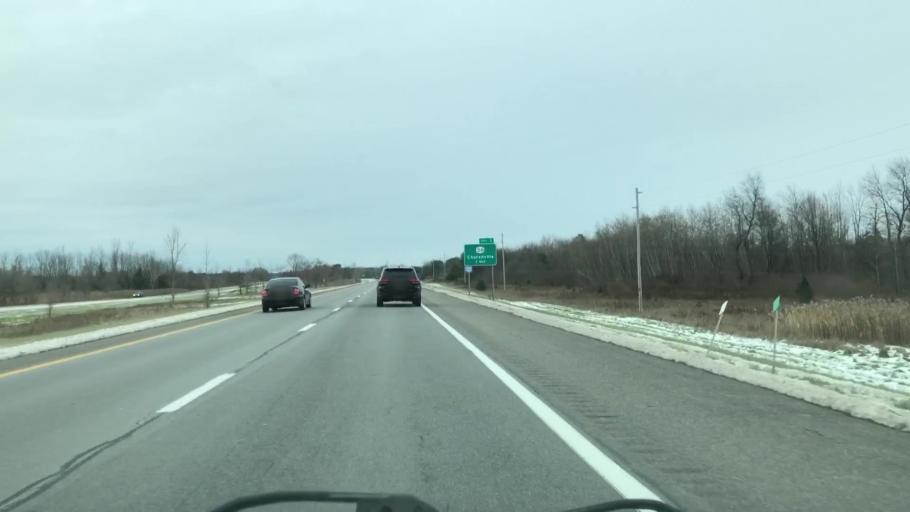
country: US
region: New York
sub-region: Monroe County
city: Churchville
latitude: 43.0874
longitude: -77.9083
